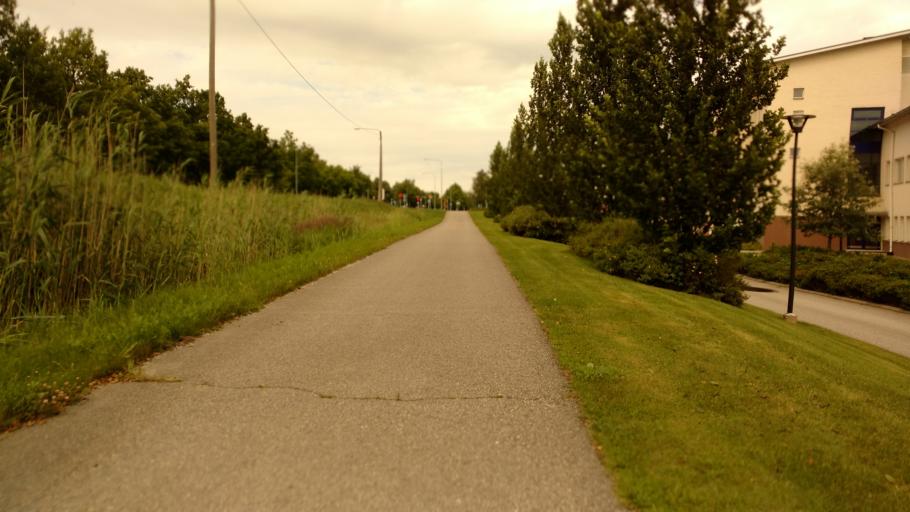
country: FI
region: Varsinais-Suomi
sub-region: Salo
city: Salo
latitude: 60.3747
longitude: 23.1351
